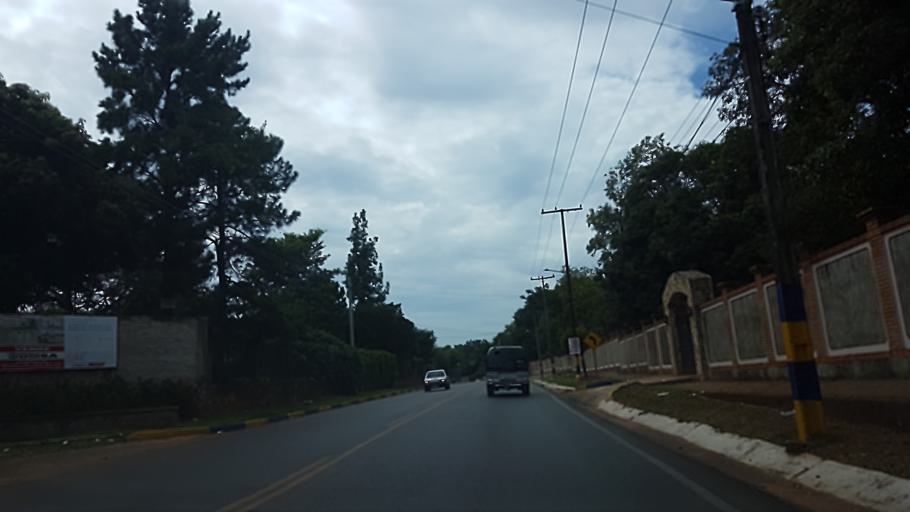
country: PY
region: Central
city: San Lorenzo
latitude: -25.2924
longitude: -57.4801
